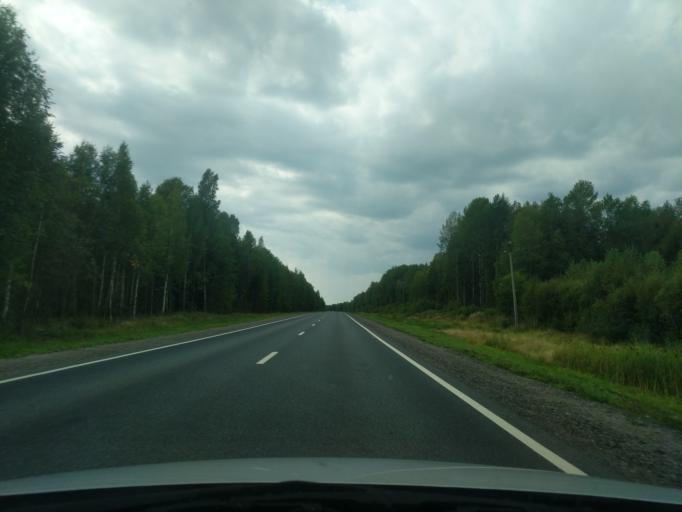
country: RU
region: Kostroma
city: Manturovo
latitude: 58.1594
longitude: 44.3915
